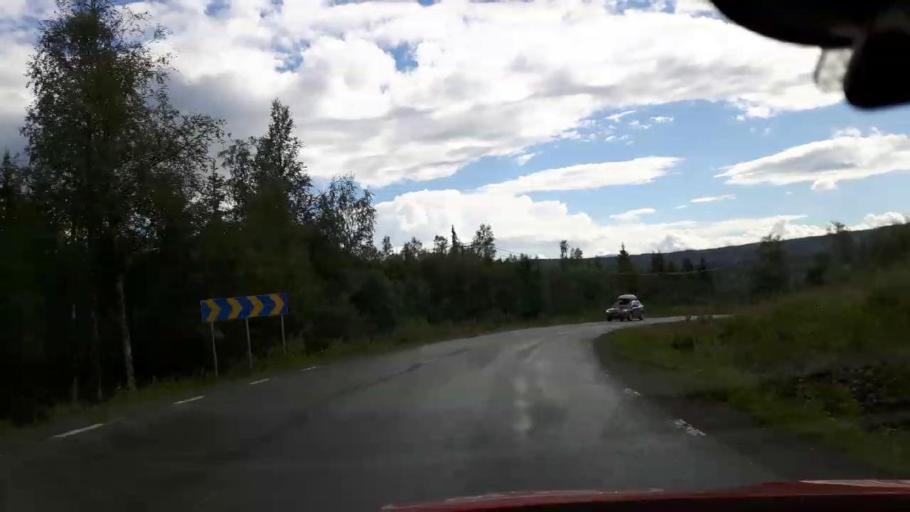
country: SE
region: Jaemtland
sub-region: Are Kommun
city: Are
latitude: 63.3206
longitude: 13.2339
